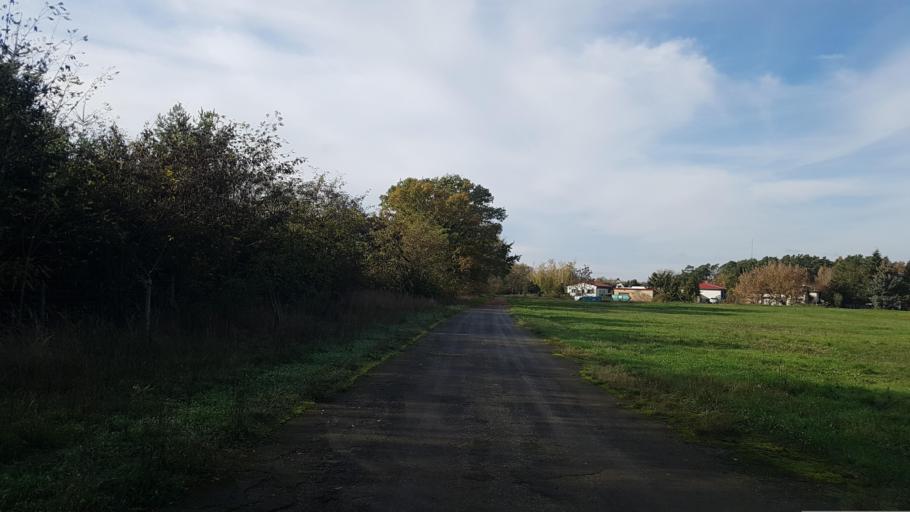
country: DE
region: Brandenburg
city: Schlieben
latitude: 51.7344
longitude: 13.3879
